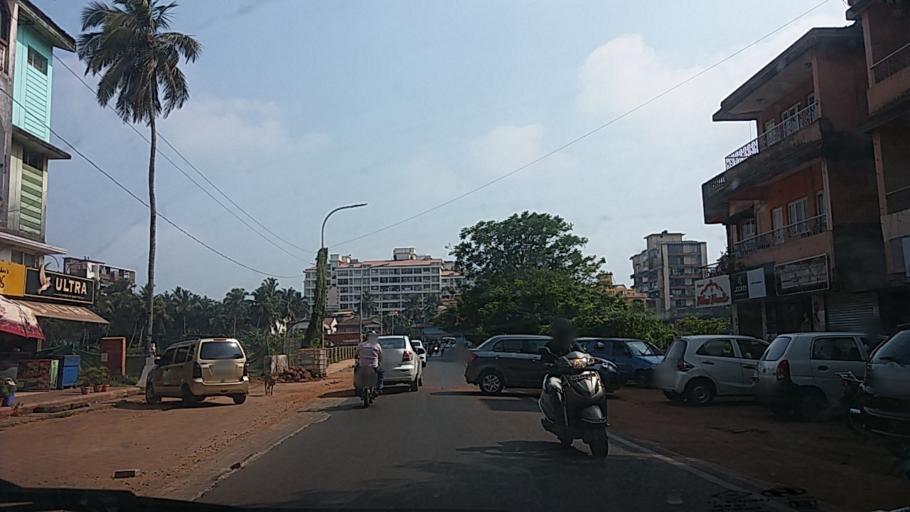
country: IN
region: Goa
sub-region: North Goa
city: Panaji
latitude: 15.4793
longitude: 73.8122
